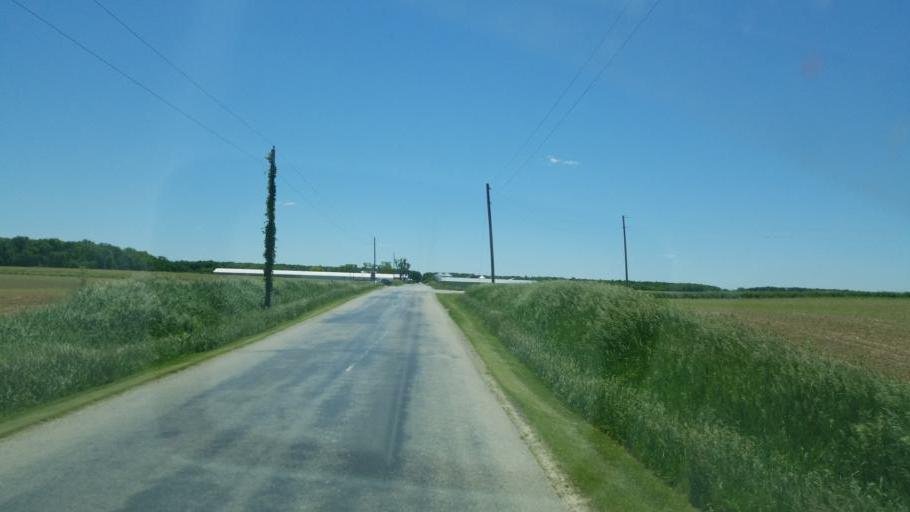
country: US
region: Ohio
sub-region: Mercer County
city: Fort Recovery
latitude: 40.3393
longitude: -84.8037
